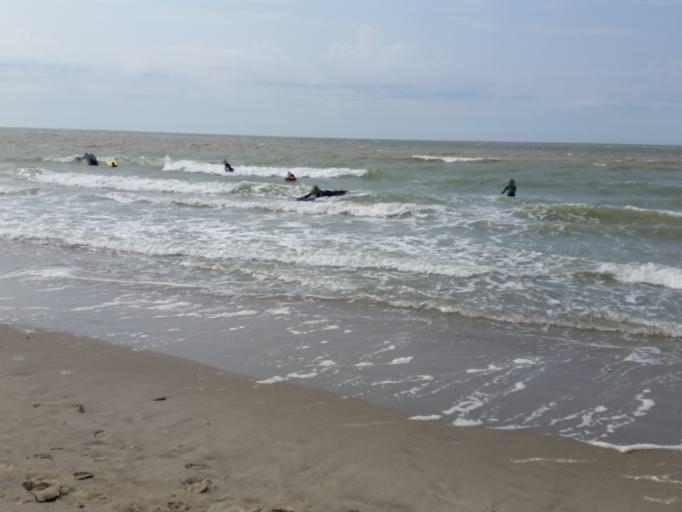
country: BE
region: Flanders
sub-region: Provincie West-Vlaanderen
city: Bredene
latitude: 51.2468
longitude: 2.9508
